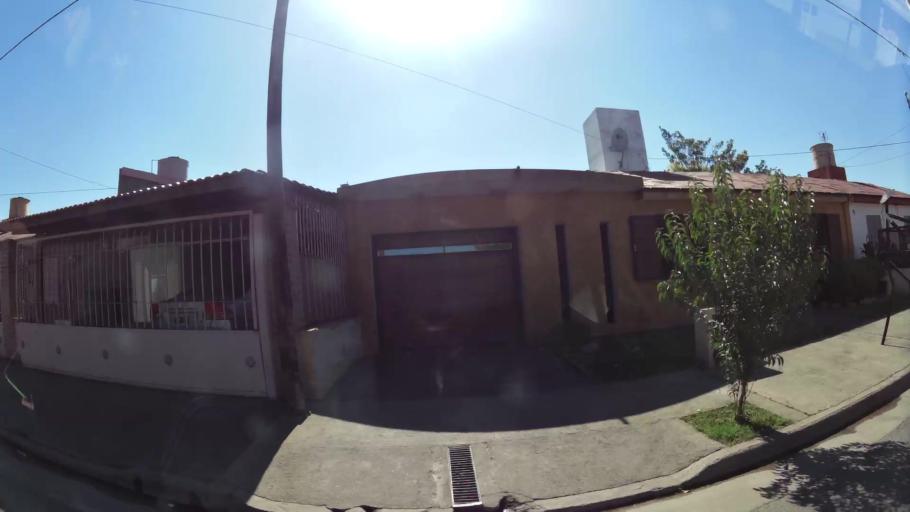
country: AR
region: Cordoba
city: Villa Allende
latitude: -31.3199
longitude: -64.2551
